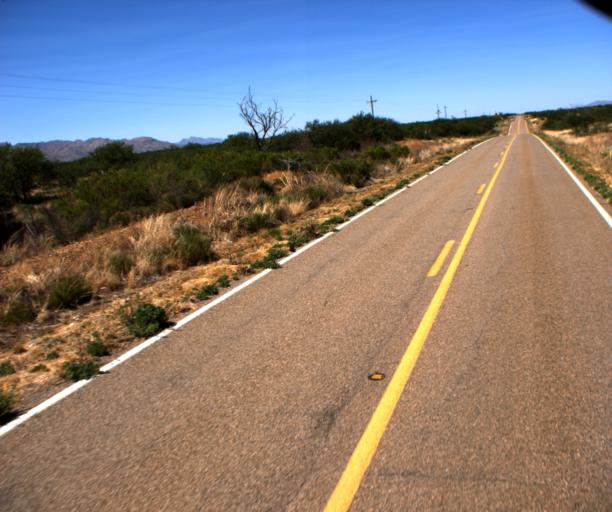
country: US
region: Arizona
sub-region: Pima County
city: Arivaca Junction
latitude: 31.6378
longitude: -111.5037
